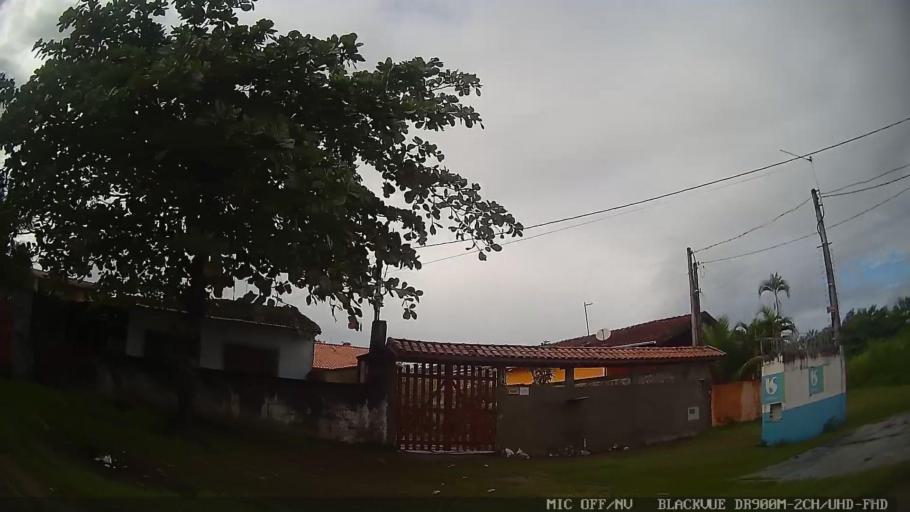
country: BR
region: Sao Paulo
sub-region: Itanhaem
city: Itanhaem
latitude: -24.2426
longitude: -46.8941
